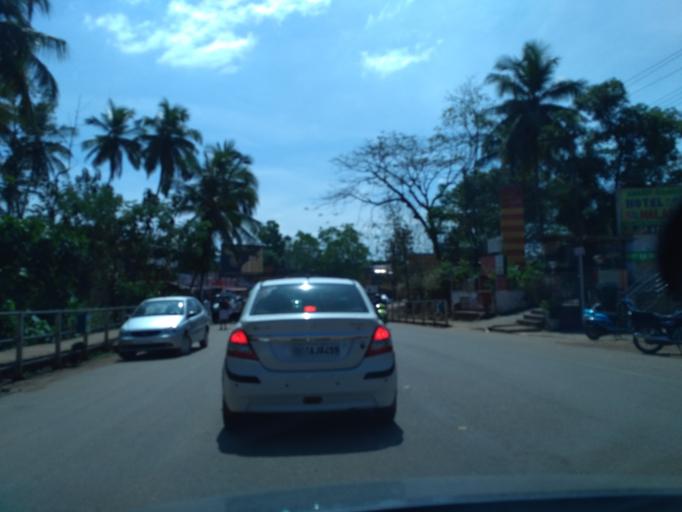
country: IN
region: Karnataka
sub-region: Dakshina Kannada
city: Sulya
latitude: 12.5629
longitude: 75.3905
